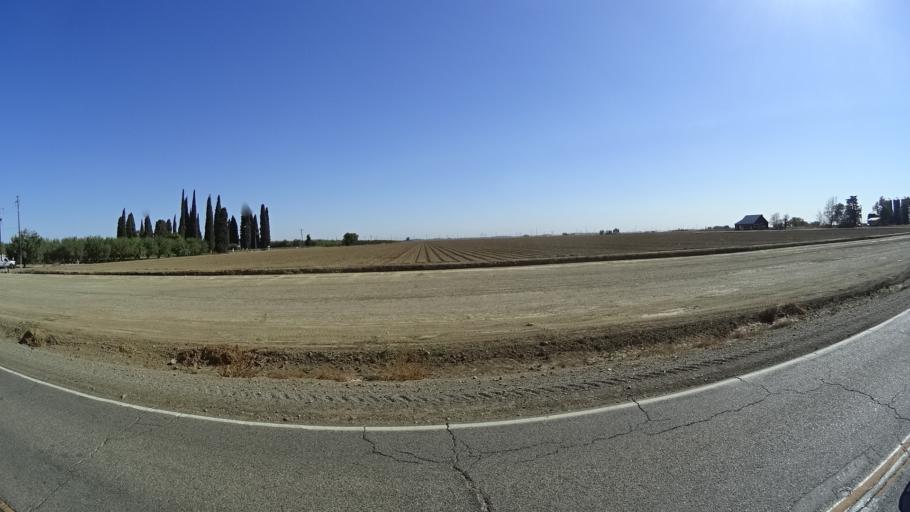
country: US
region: California
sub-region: Yolo County
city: Cottonwood
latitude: 38.6491
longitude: -121.9715
